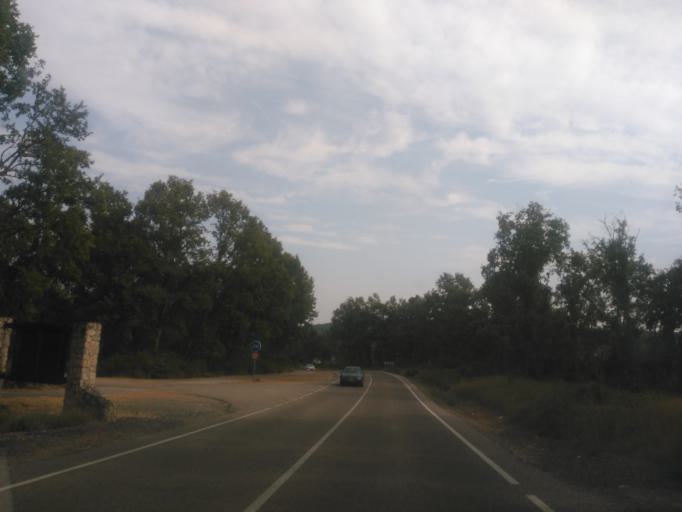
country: ES
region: Castille and Leon
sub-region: Provincia de Zamora
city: Galende
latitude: 42.0863
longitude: -6.6457
